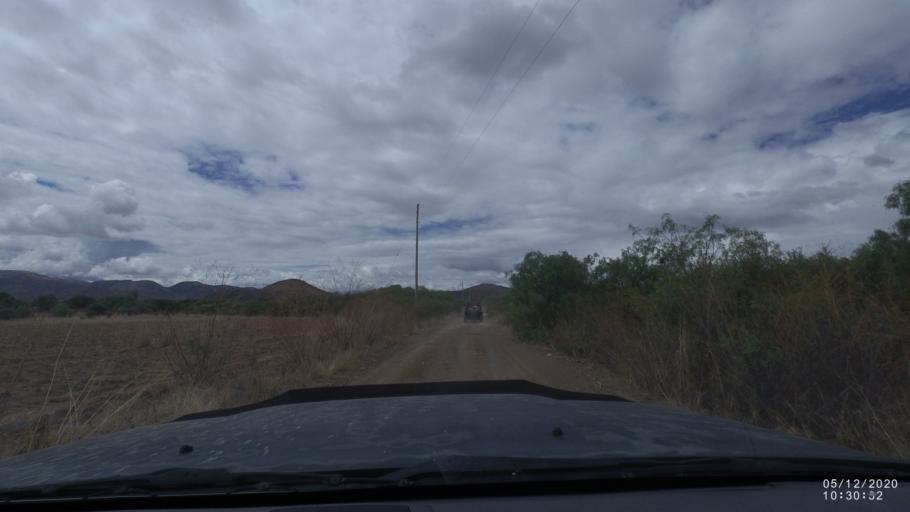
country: BO
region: Cochabamba
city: Sipe Sipe
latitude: -17.5432
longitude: -66.2687
